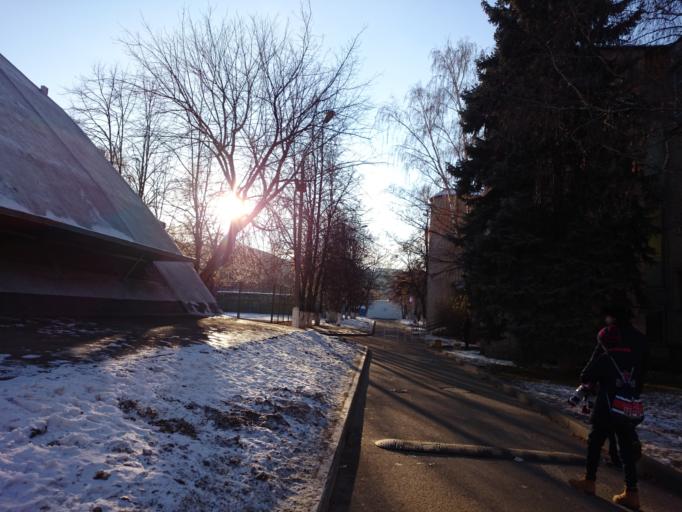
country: RU
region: Moscow
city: Sokol
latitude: 55.7938
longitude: 37.5377
